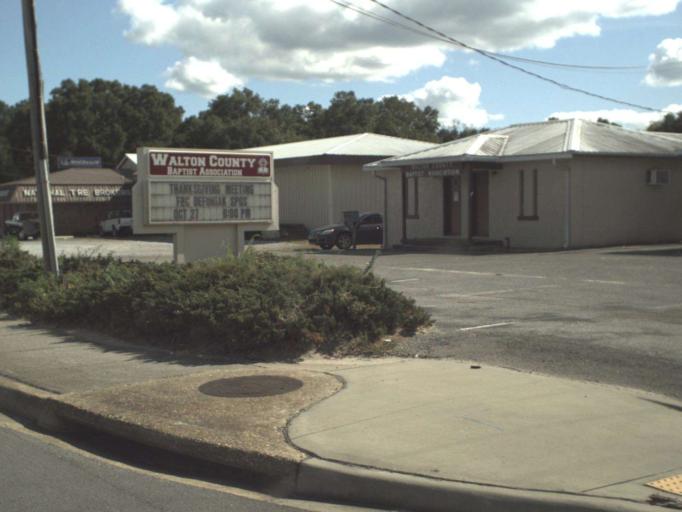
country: US
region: Florida
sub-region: Walton County
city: DeFuniak Springs
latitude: 30.7277
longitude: -86.1331
